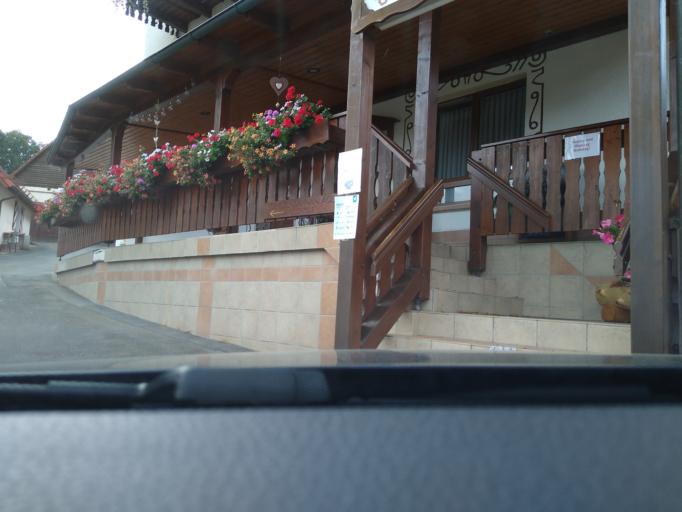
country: DE
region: Bavaria
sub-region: Upper Franconia
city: Obertrubach
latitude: 49.7079
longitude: 11.3722
